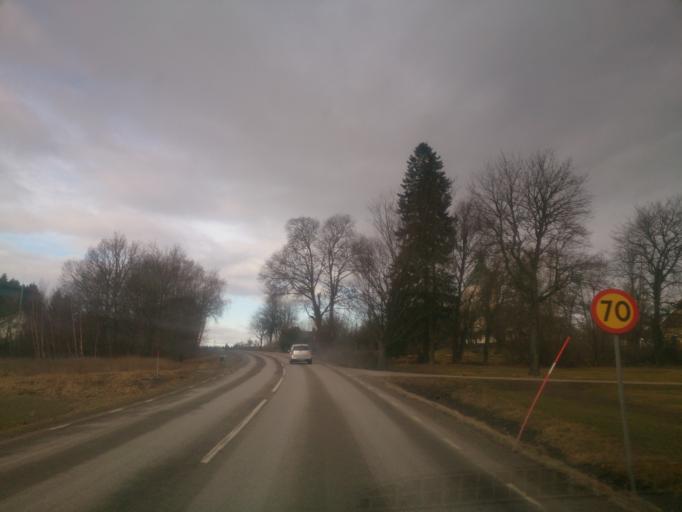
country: SE
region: OEstergoetland
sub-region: Motala Kommun
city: Stenstorp
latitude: 58.5155
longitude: 15.0922
